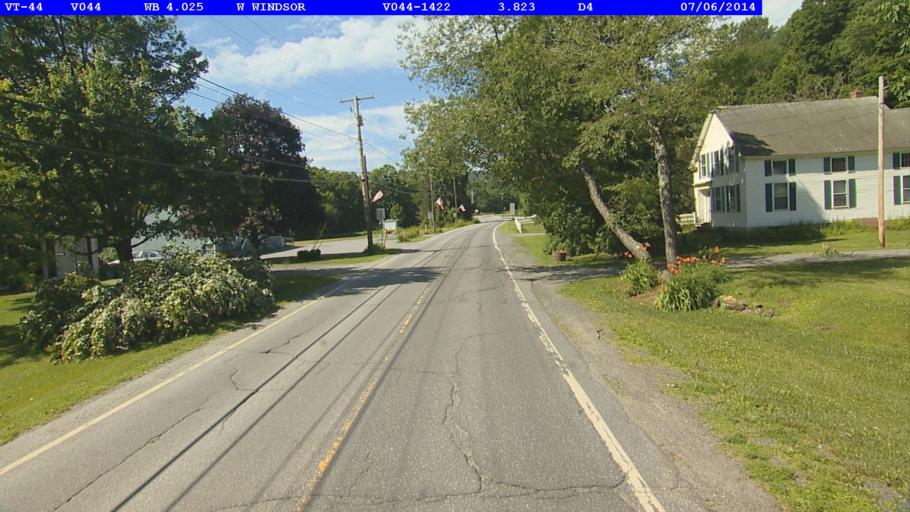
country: US
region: Vermont
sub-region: Windsor County
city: Windsor
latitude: 43.4650
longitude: -72.4746
